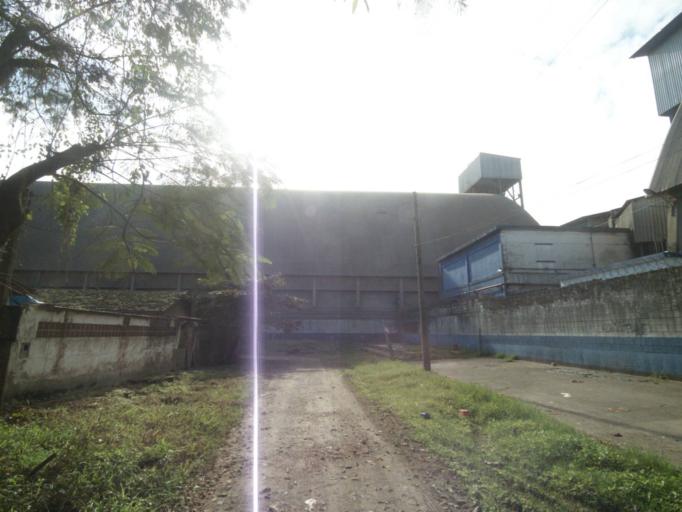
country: BR
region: Parana
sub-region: Paranagua
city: Paranagua
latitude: -25.5079
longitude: -48.5236
